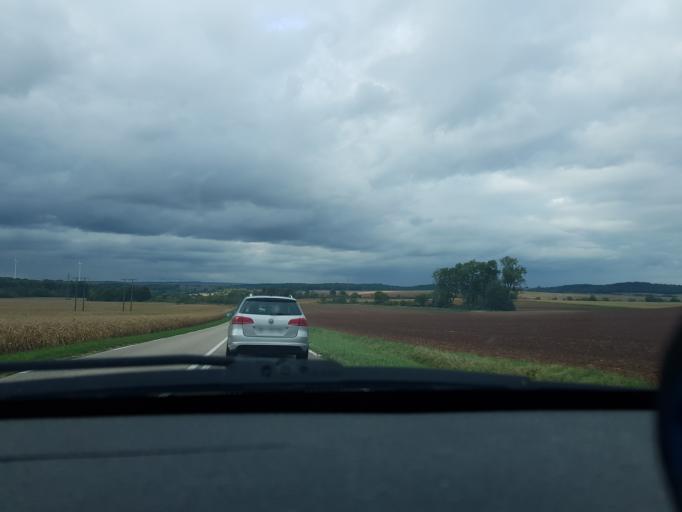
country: FR
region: Lorraine
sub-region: Departement de la Moselle
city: Morhange
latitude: 48.9449
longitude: 6.6107
